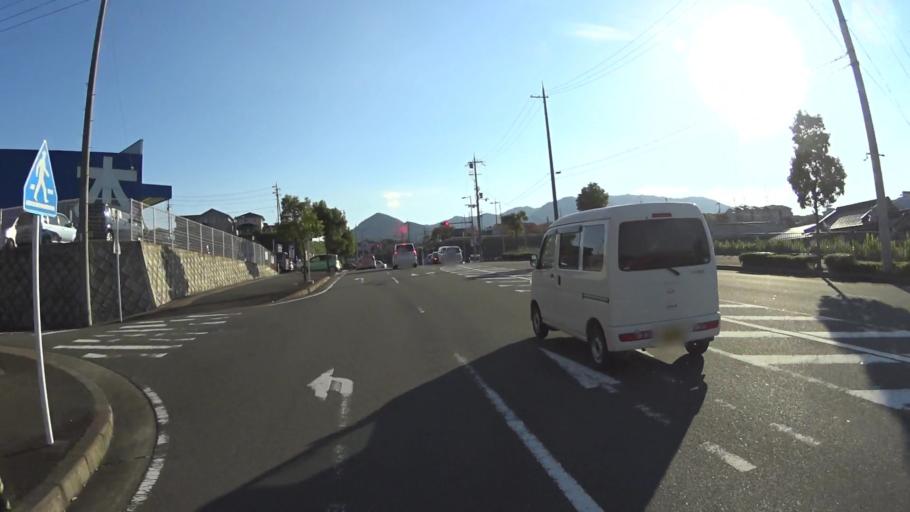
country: JP
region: Kyoto
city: Fukuchiyama
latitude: 35.2918
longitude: 135.1228
